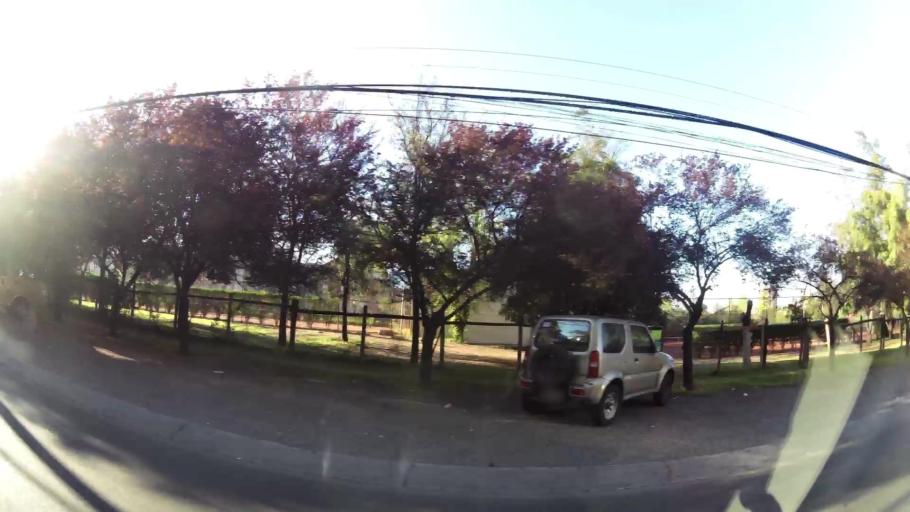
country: CL
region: Santiago Metropolitan
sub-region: Provincia de Santiago
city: Villa Presidente Frei, Nunoa, Santiago, Chile
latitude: -33.4059
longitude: -70.5836
